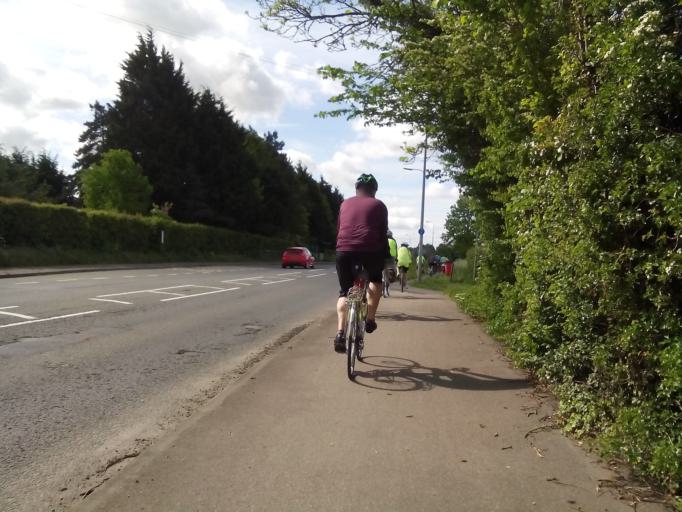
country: GB
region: England
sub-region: Cambridgeshire
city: Harston
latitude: 52.1495
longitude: 0.0915
